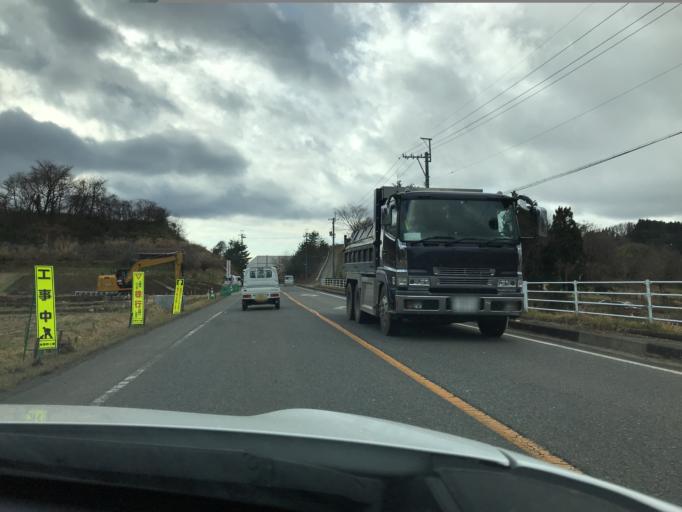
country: JP
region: Fukushima
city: Nihommatsu
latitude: 37.6010
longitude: 140.5813
